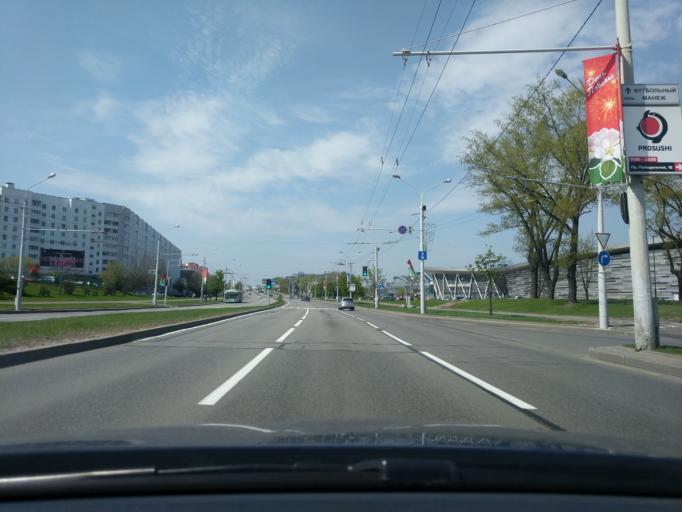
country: BY
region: Minsk
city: Minsk
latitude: 53.9305
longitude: 27.5121
